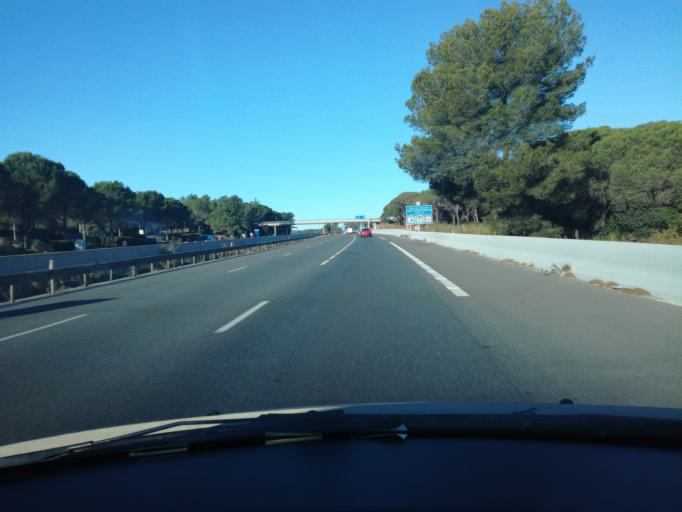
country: FR
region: Provence-Alpes-Cote d'Azur
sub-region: Departement du Var
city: Puget-sur-Argens
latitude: 43.4646
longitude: 6.6770
